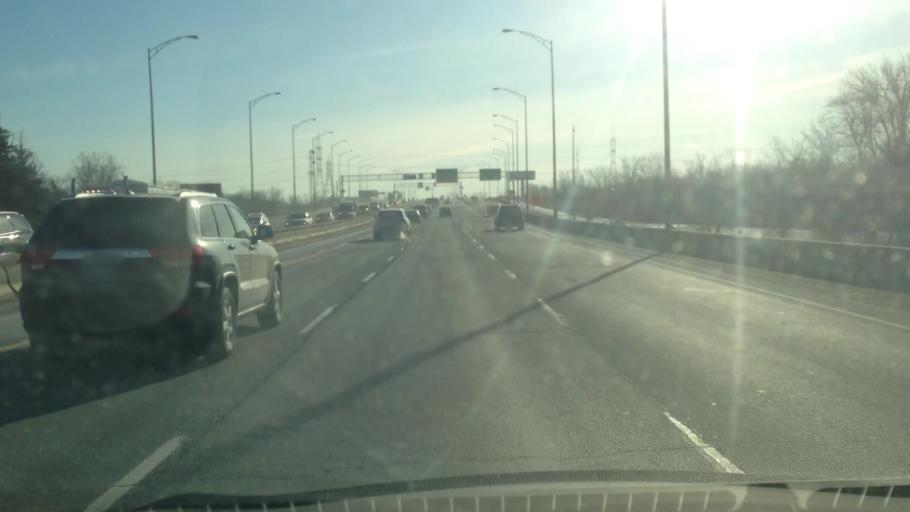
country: CA
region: Quebec
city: Dorval
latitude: 45.5093
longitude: -73.7626
